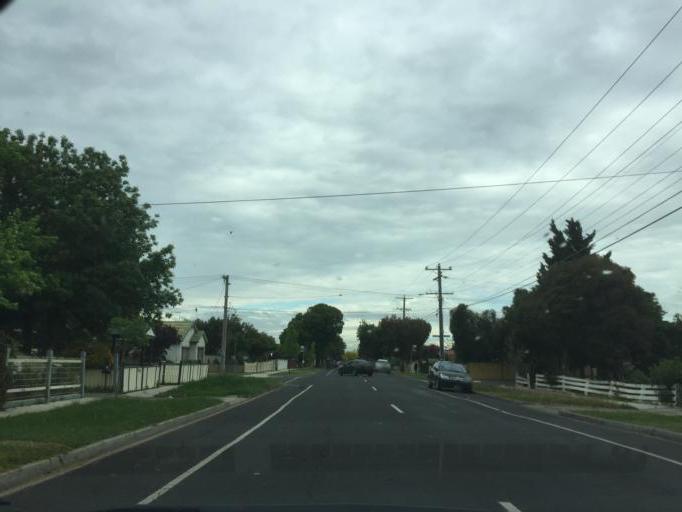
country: AU
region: Victoria
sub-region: Maribyrnong
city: Braybrook
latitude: -37.7800
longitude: 144.8423
